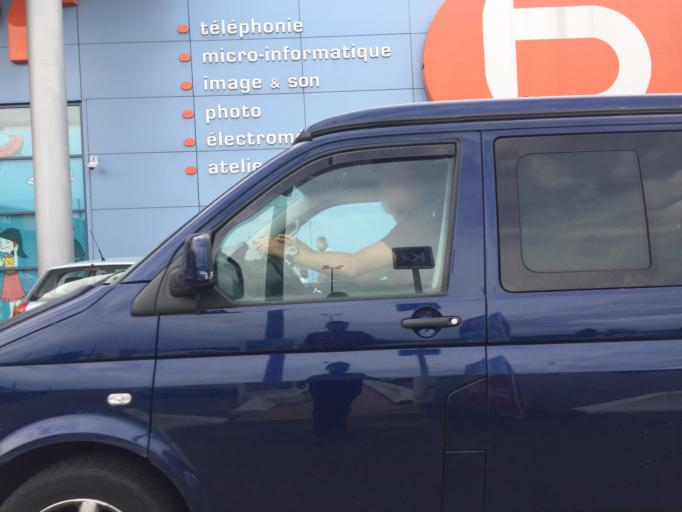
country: FR
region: Rhone-Alpes
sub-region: Departement de l'Ain
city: Beynost
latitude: 45.8237
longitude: 4.9988
